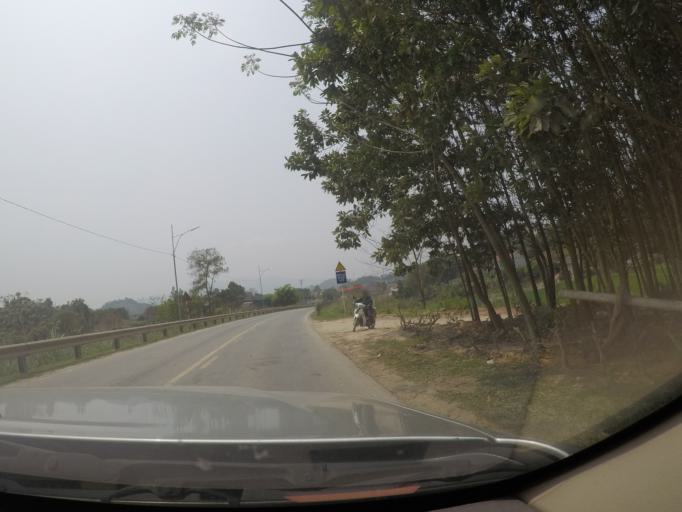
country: VN
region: Thanh Hoa
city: Thi Tran Yen Cat
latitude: 19.6685
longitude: 105.4509
